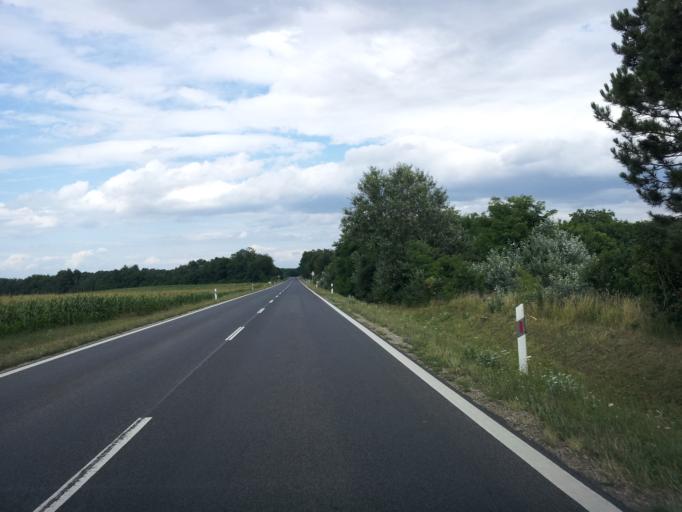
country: HU
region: Vas
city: Janoshaza
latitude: 47.1064
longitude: 17.0930
